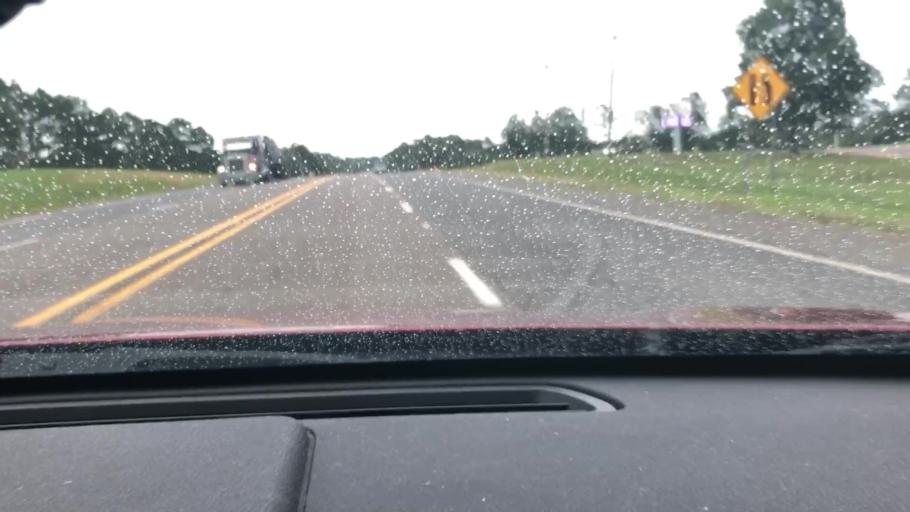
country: US
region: Arkansas
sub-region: Lafayette County
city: Lewisville
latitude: 33.3583
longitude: -93.5580
